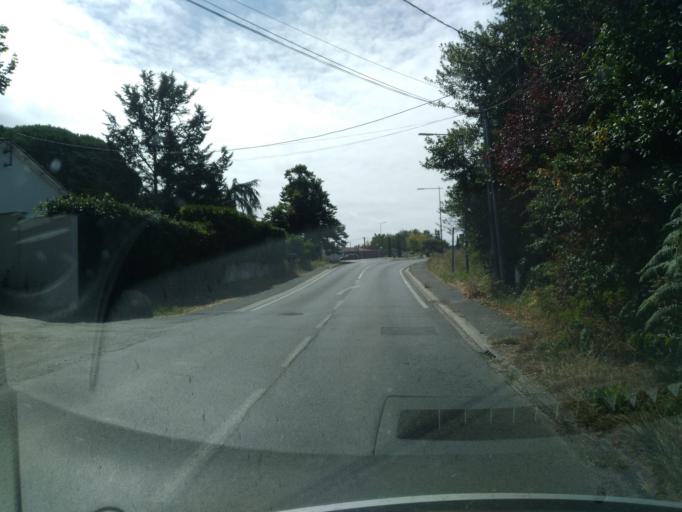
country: FR
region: Poitou-Charentes
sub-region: Departement de la Charente-Maritime
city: Vaux-sur-Mer
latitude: 45.6645
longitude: -1.0726
